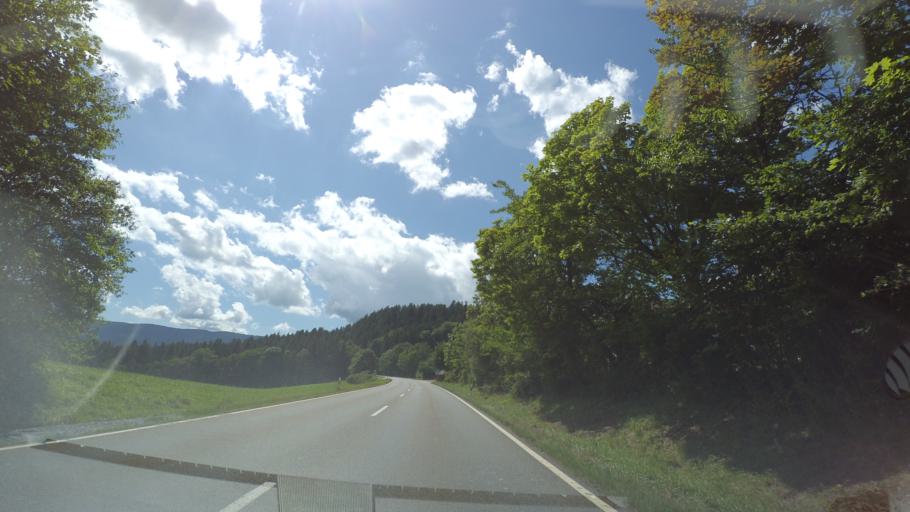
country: DE
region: Bavaria
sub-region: Lower Bavaria
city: Kollnburg
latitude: 49.0491
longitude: 12.8677
